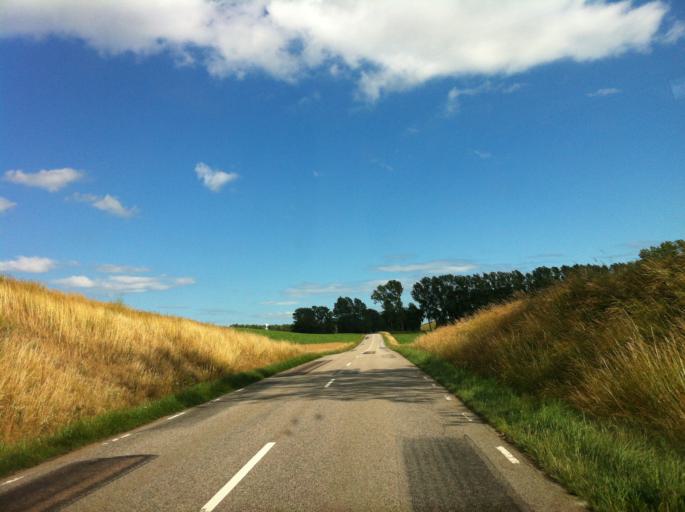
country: SE
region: Skane
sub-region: Ystads Kommun
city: Kopingebro
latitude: 55.4173
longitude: 13.9987
